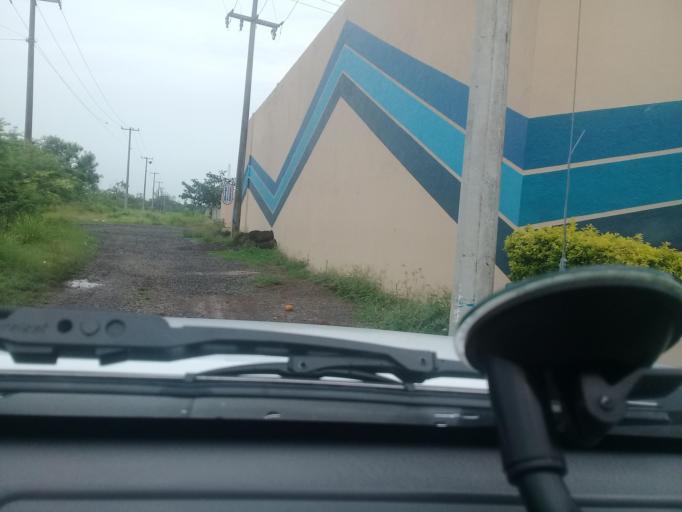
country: MX
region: Veracruz
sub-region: Puente Nacional
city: Cabezas
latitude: 19.3691
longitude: -96.3860
